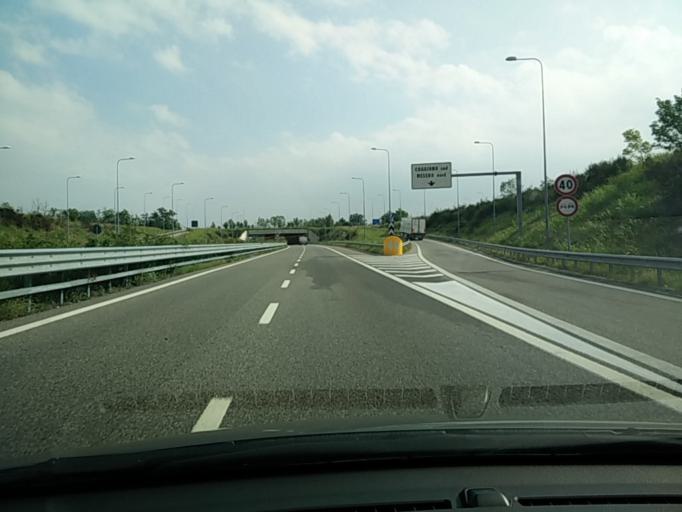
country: IT
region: Lombardy
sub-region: Citta metropolitana di Milano
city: Casate
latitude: 45.5052
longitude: 8.8317
